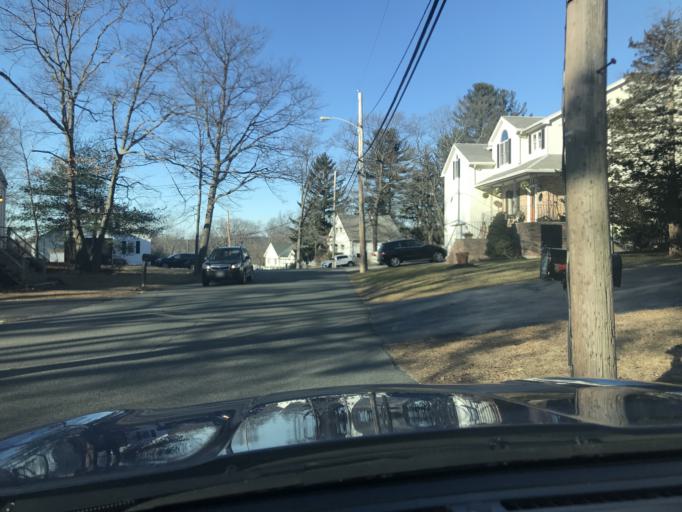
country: US
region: Massachusetts
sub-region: Essex County
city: Saugus
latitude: 42.4865
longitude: -71.0096
